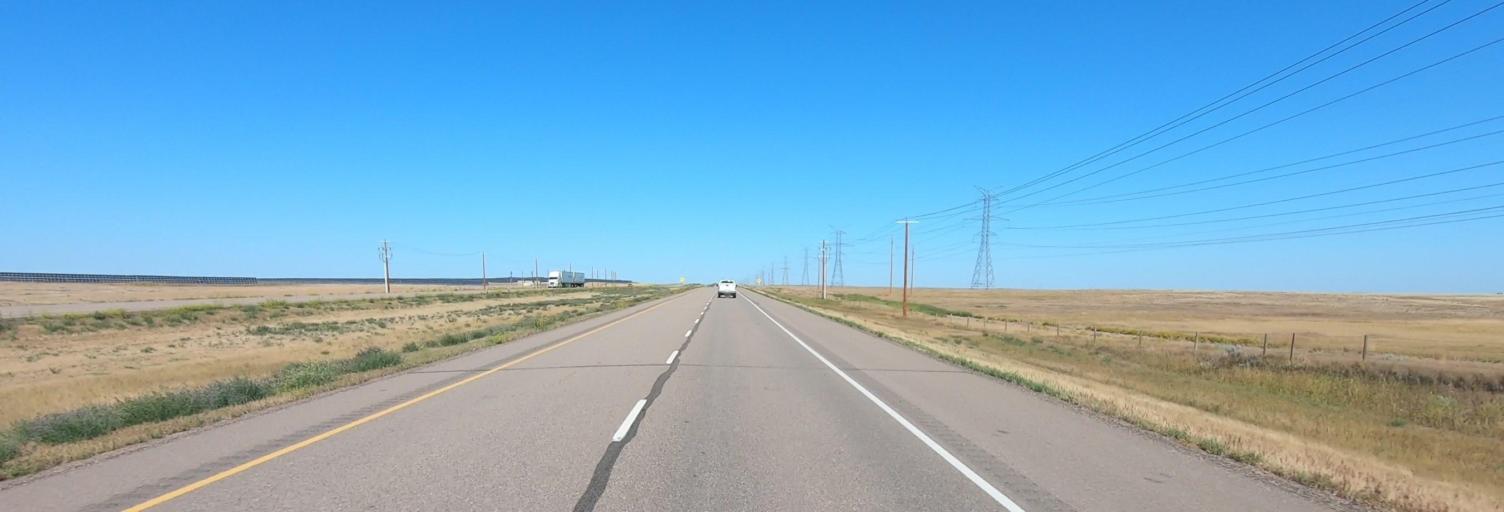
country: CA
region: Alberta
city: Bow Island
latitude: 50.2681
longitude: -111.2600
